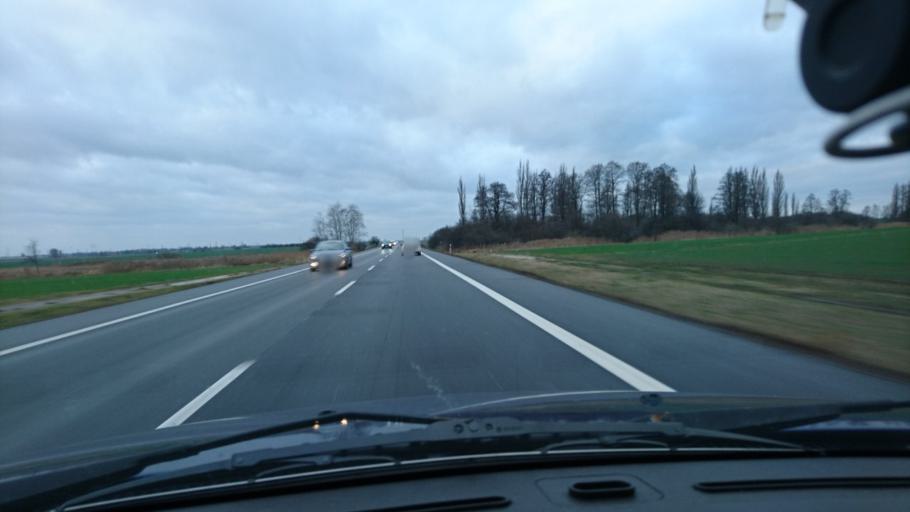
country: PL
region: Opole Voivodeship
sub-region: Powiat kluczborski
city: Kluczbork
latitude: 50.9842
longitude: 18.2419
